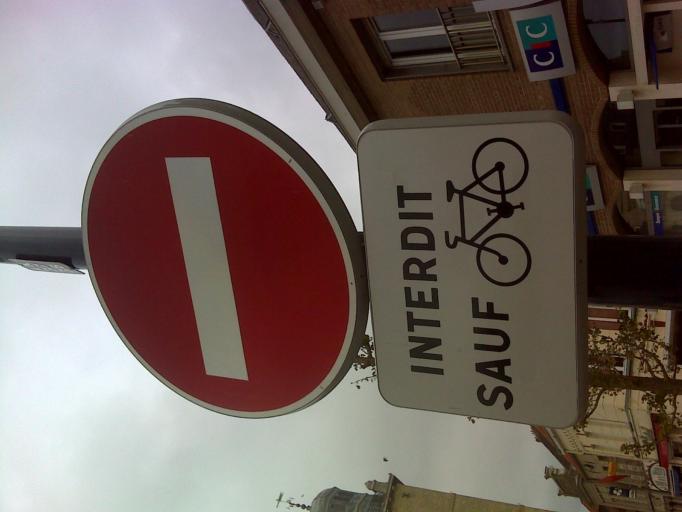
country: FR
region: Nord-Pas-de-Calais
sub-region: Departement du Nord
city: Gravelines
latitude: 50.9863
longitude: 2.1264
